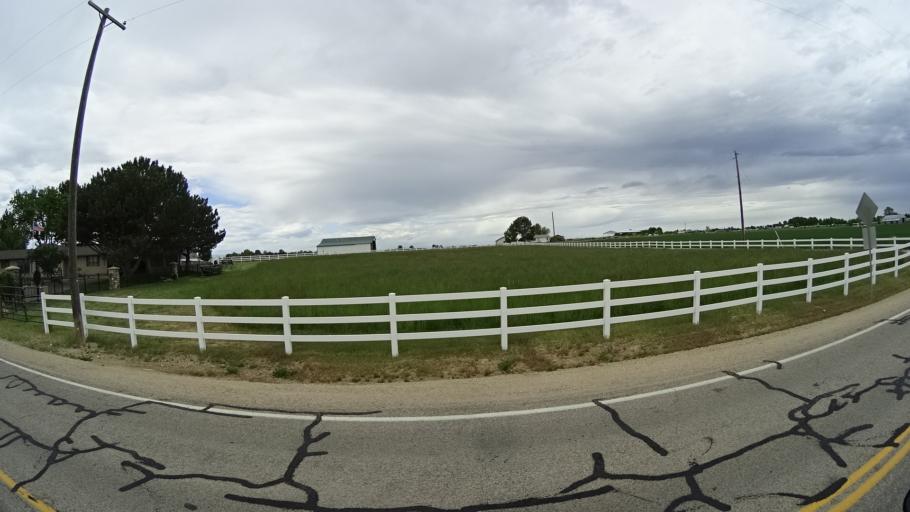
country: US
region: Idaho
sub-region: Ada County
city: Meridian
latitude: 43.5680
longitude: -116.4138
